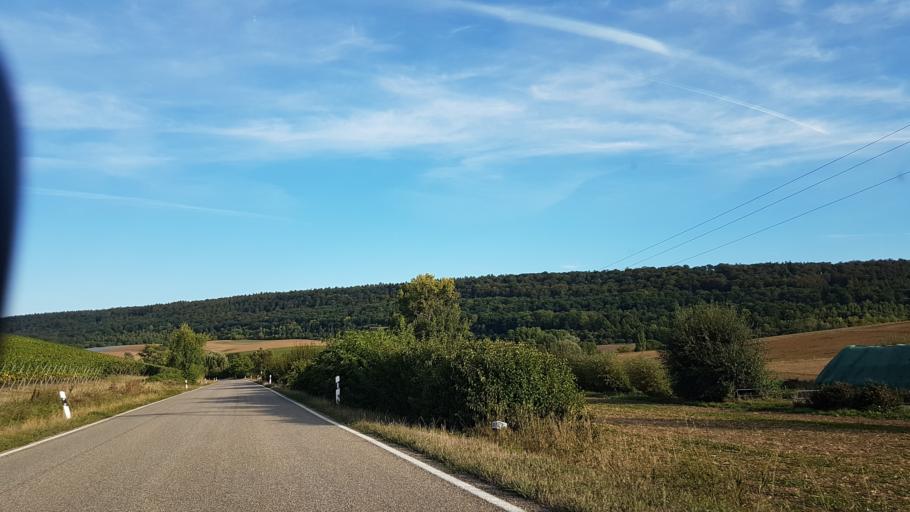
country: DE
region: Baden-Wuerttemberg
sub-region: Regierungsbezirk Stuttgart
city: Eberstadt
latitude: 49.1768
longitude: 9.3053
